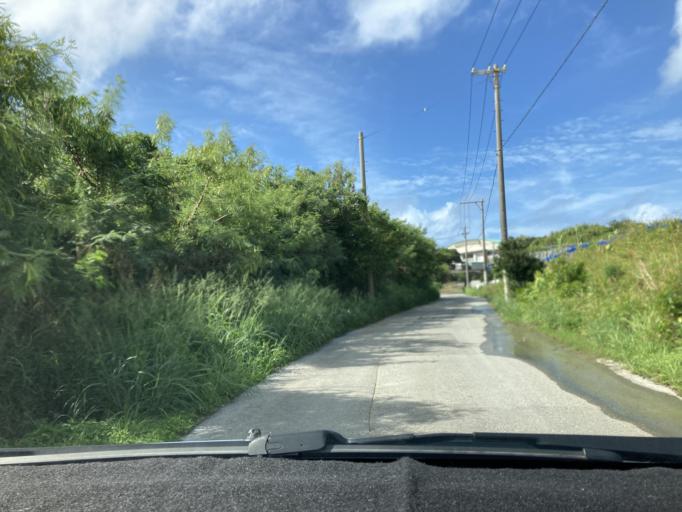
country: JP
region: Okinawa
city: Itoman
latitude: 26.0955
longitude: 127.6665
